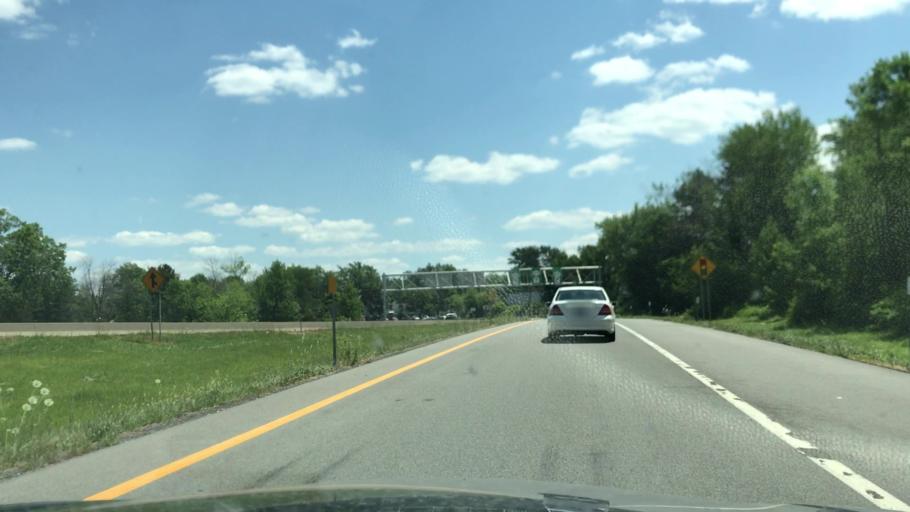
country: US
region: New York
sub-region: Erie County
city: West Seneca
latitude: 42.8427
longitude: -78.7568
